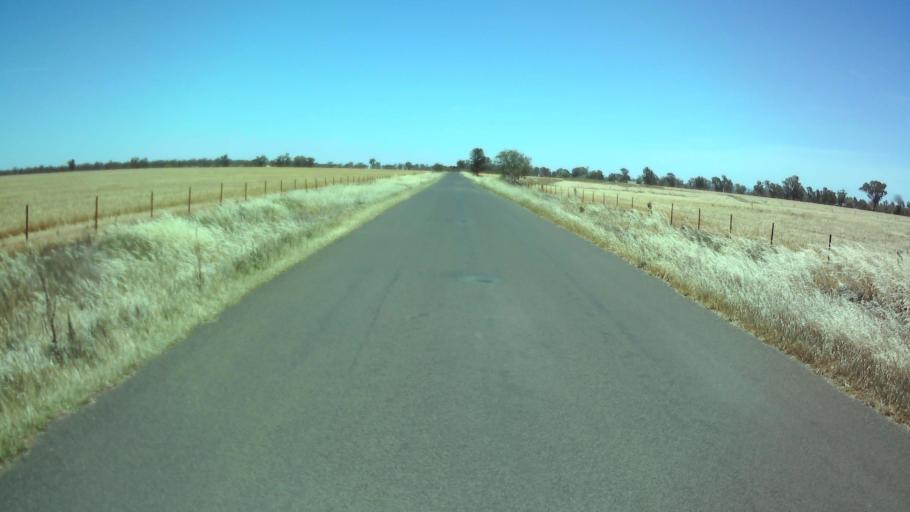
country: AU
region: New South Wales
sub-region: Weddin
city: Grenfell
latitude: -34.0506
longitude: 147.7817
